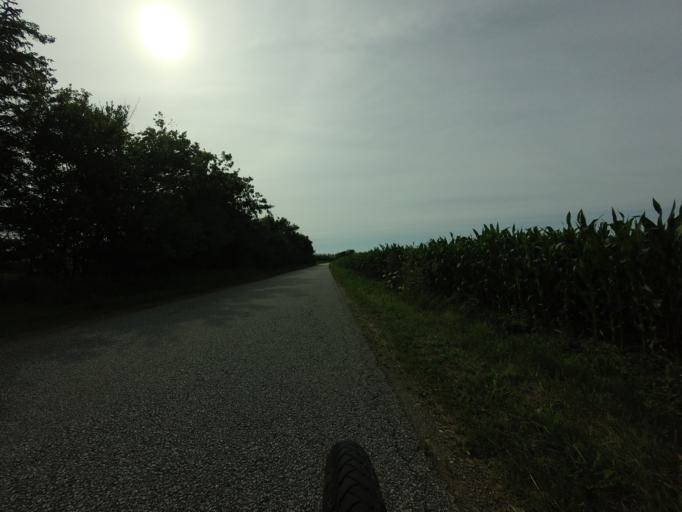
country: DK
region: North Denmark
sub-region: Hjorring Kommune
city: Hjorring
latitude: 57.4342
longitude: 9.8814
